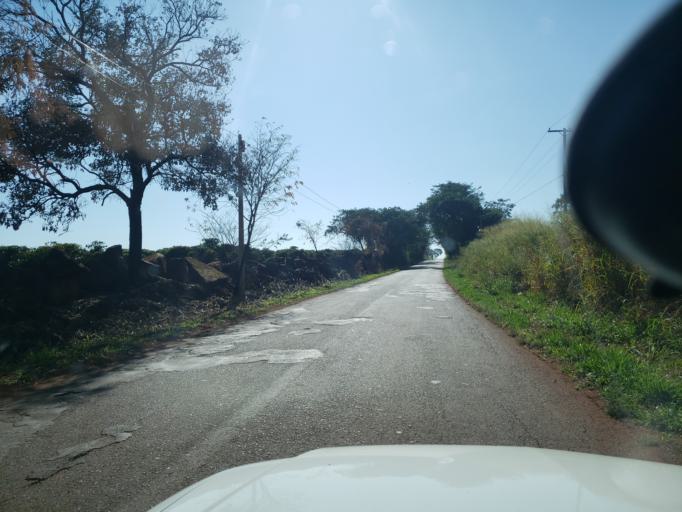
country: BR
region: Sao Paulo
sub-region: Moji-Guacu
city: Mogi-Gaucu
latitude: -22.3434
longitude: -46.8903
